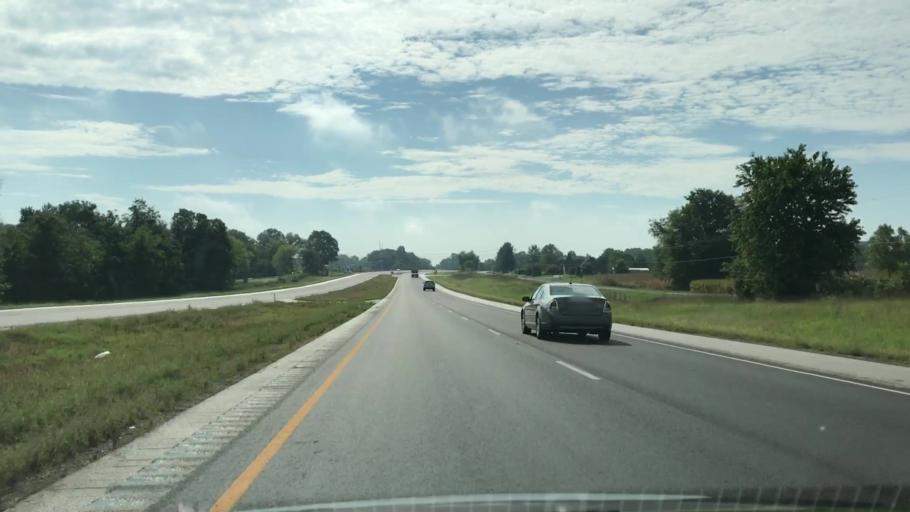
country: US
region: Kentucky
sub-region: Warren County
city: Plano
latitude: 36.8837
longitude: -86.3634
